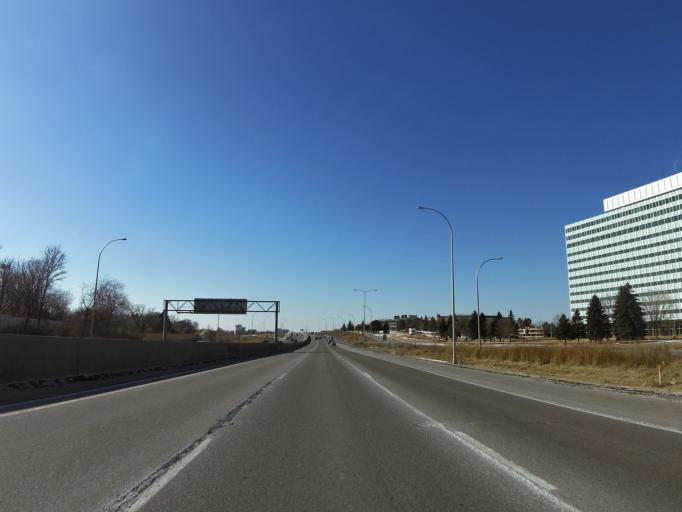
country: US
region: Minnesota
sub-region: Ramsey County
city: Maplewood
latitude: 44.9489
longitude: -92.9935
